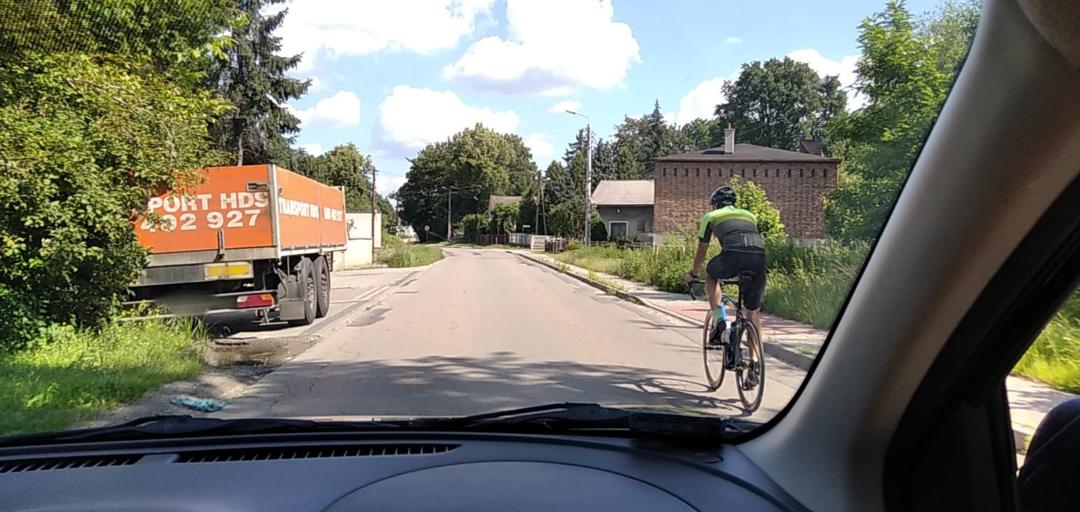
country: PL
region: Silesian Voivodeship
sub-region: Powiat bedzinski
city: Sarnow
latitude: 50.3880
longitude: 19.1368
